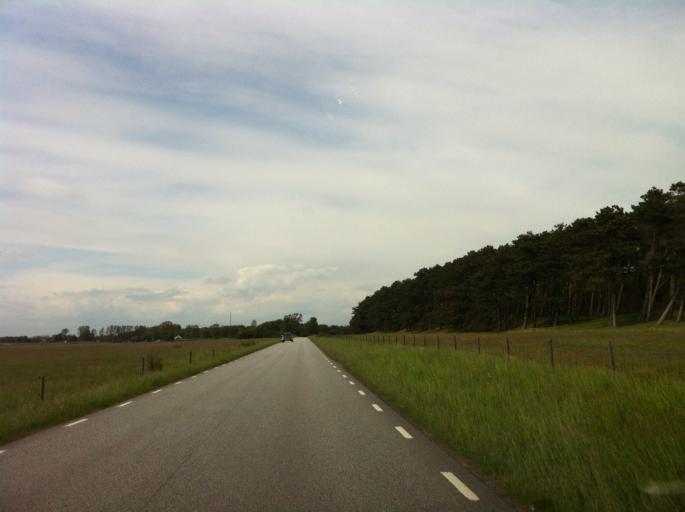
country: SE
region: Skane
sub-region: Kavlinge Kommun
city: Hofterup
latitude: 55.8080
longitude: 12.9370
